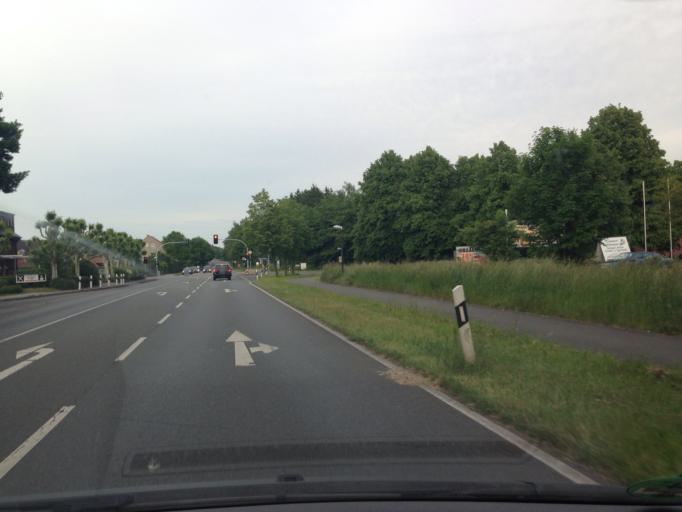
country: DE
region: North Rhine-Westphalia
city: Ludinghausen
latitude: 51.7647
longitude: 7.4126
